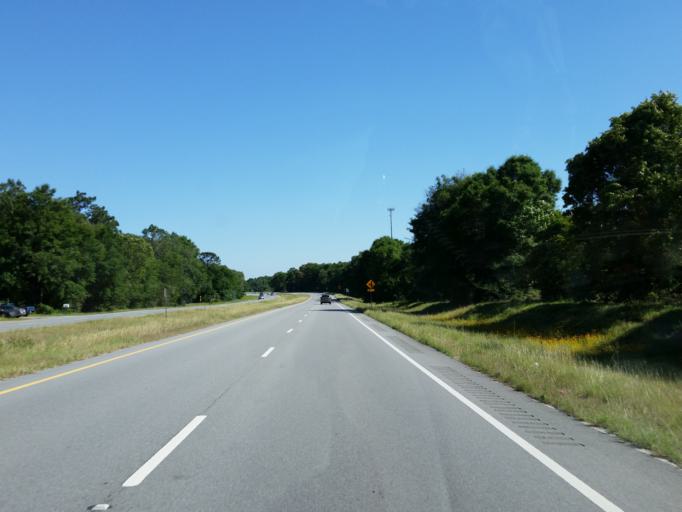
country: US
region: Georgia
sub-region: Lowndes County
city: Valdosta
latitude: 30.6960
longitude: -83.2102
